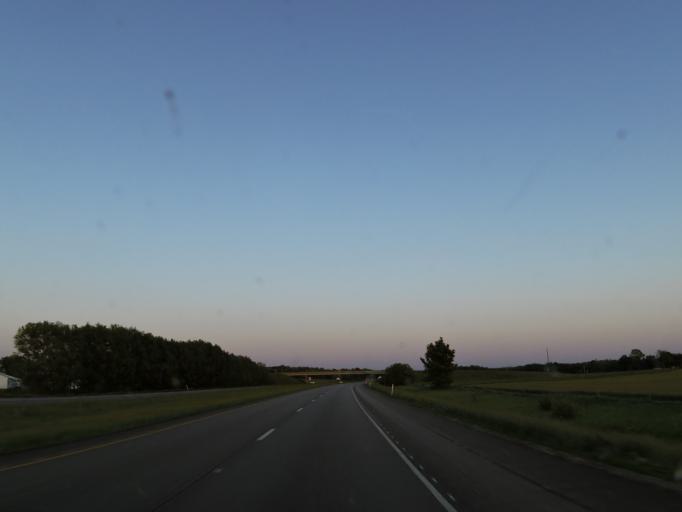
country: US
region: Indiana
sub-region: Montgomery County
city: Crawfordsville
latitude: 40.0578
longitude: -86.8274
